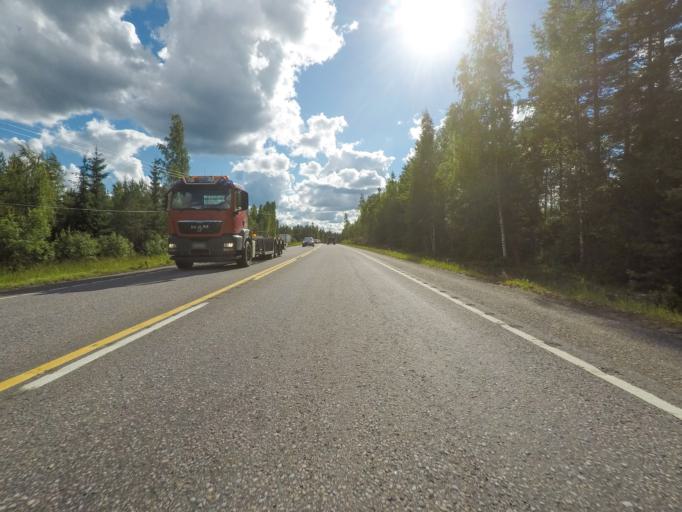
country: FI
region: Uusimaa
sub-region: Helsinki
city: Nurmijaervi
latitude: 60.5419
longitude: 24.7194
